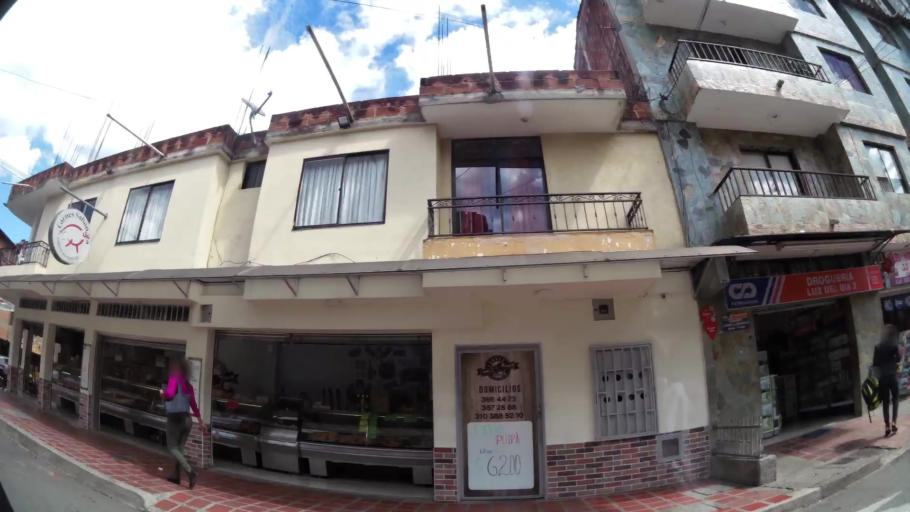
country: CO
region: Antioquia
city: Sabaneta
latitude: 6.1500
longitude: -75.6225
